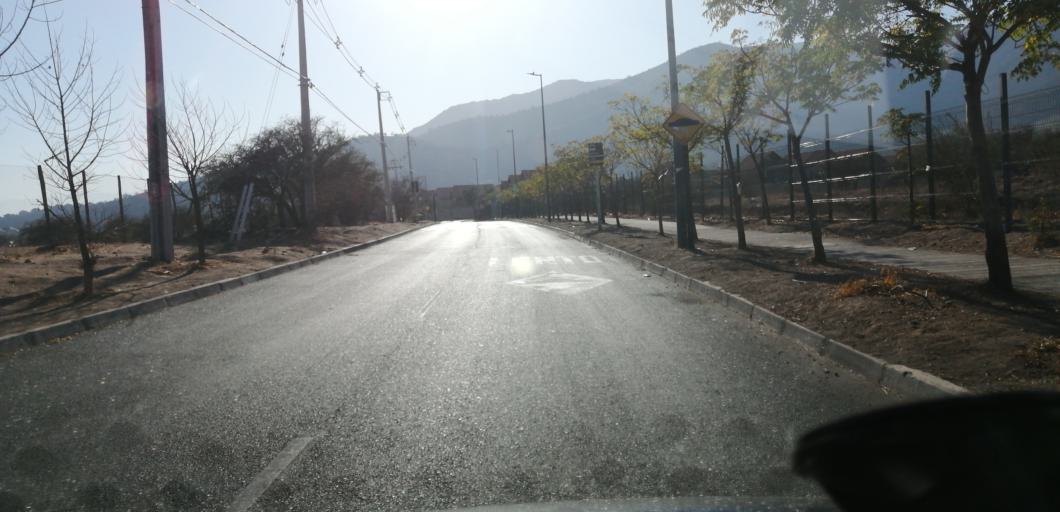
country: CL
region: Santiago Metropolitan
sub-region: Provincia de Santiago
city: Lo Prado
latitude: -33.4641
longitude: -70.8610
